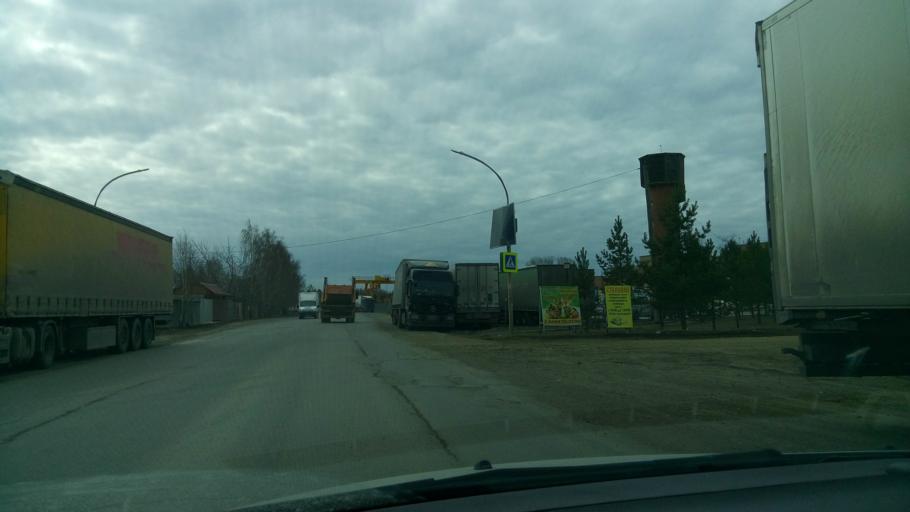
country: RU
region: Sverdlovsk
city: Verkhnyaya Pyshma
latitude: 56.9569
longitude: 60.6683
